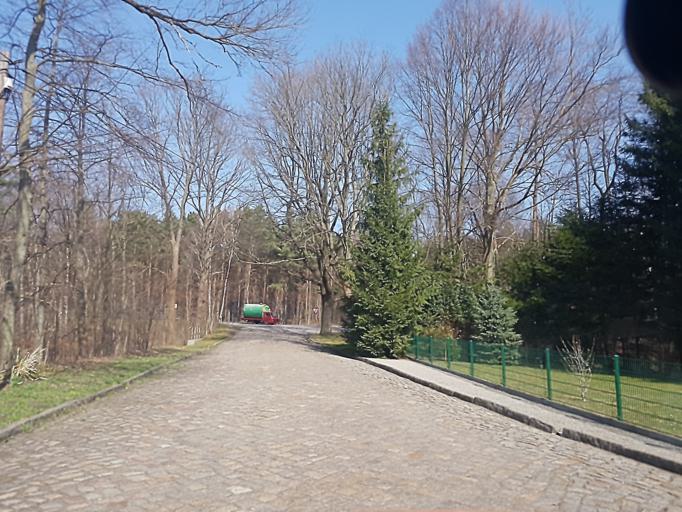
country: DE
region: Brandenburg
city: Tschernitz
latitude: 51.6265
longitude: 14.5789
